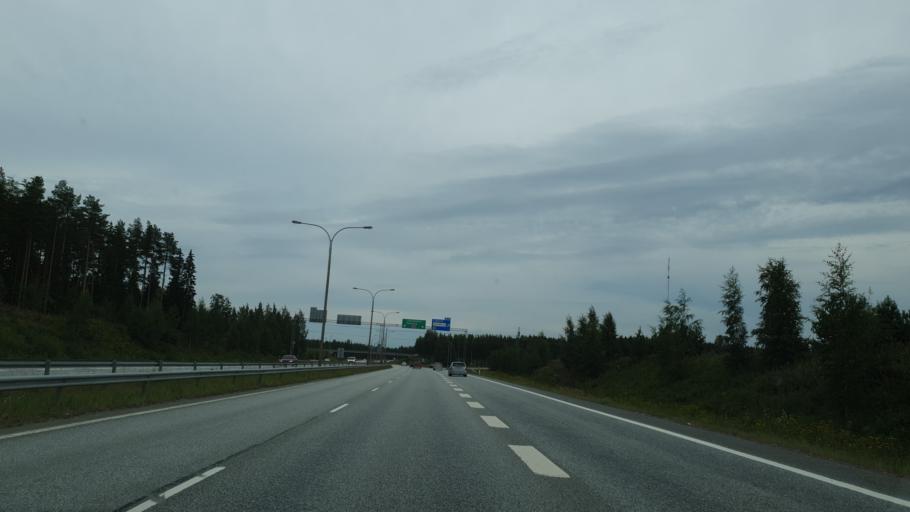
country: FI
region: North Karelia
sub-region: Joensuu
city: Joensuu
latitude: 62.5941
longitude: 29.8046
